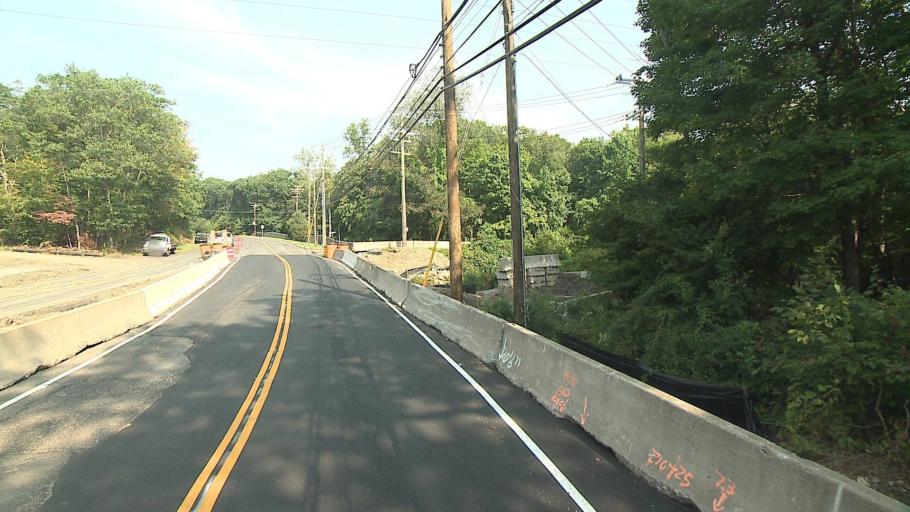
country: US
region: Connecticut
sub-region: Fairfield County
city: Westport
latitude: 41.1893
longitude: -73.3703
